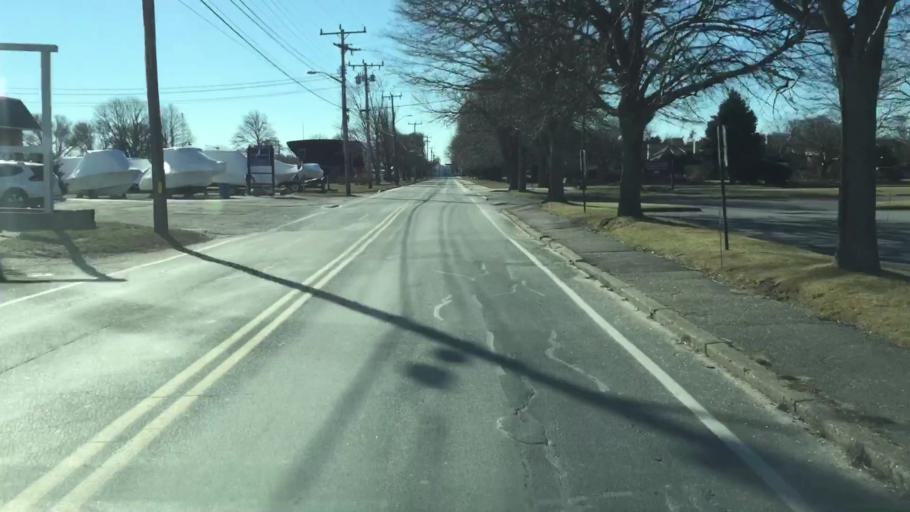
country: US
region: Massachusetts
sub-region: Barnstable County
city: Falmouth
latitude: 41.5513
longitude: -70.6030
